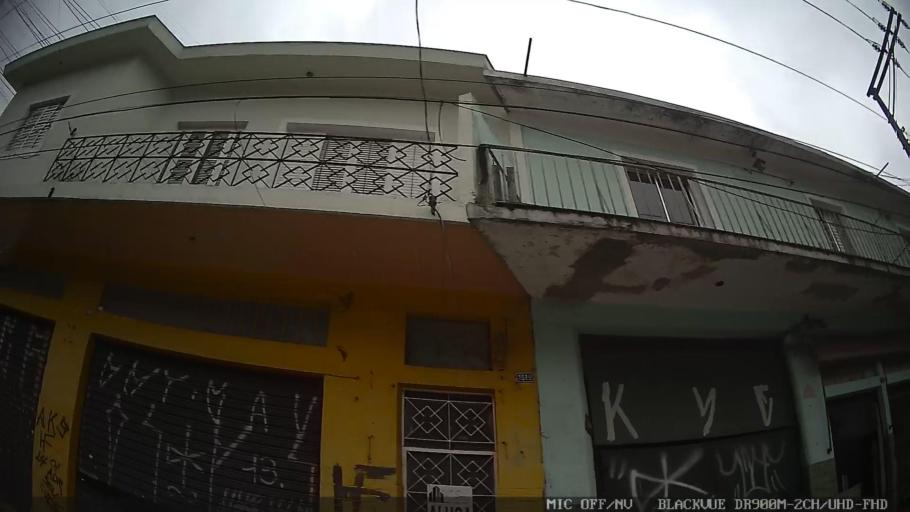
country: BR
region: Sao Paulo
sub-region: Osasco
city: Osasco
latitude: -23.4942
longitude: -46.7449
